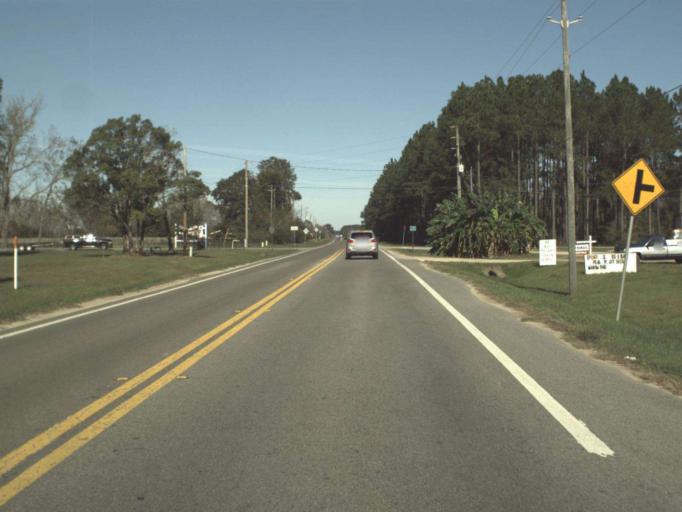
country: US
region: Florida
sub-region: Okaloosa County
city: Crestview
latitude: 30.7997
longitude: -86.6809
